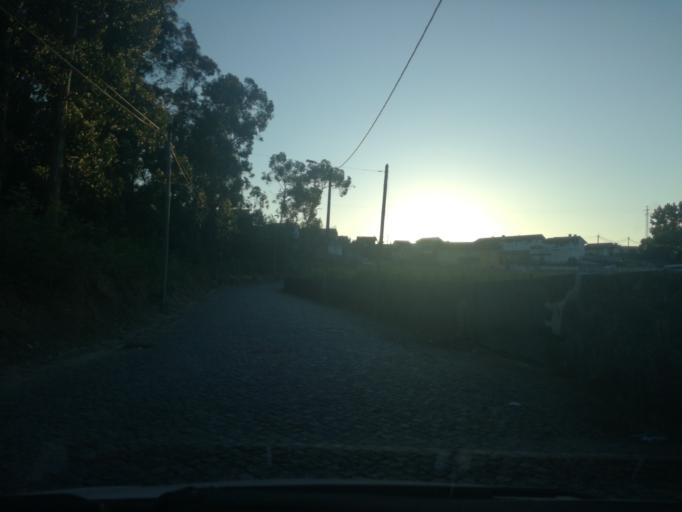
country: PT
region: Porto
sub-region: Maia
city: Nogueira
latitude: 41.2497
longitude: -8.6041
